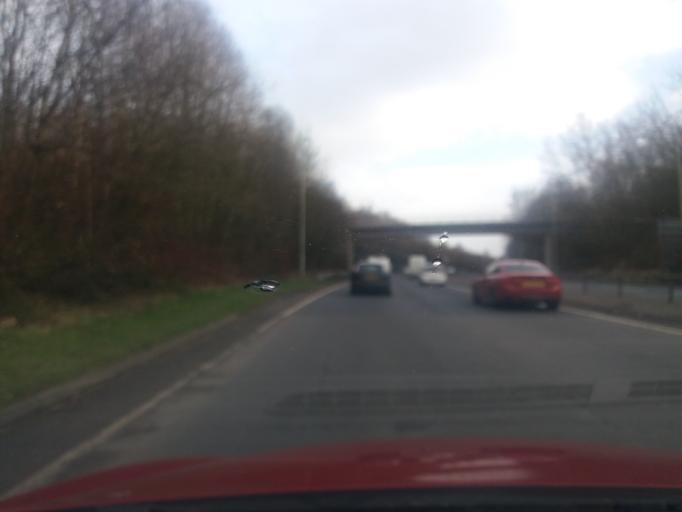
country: GB
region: England
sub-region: Lancashire
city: Preston
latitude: 53.7423
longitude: -2.6822
